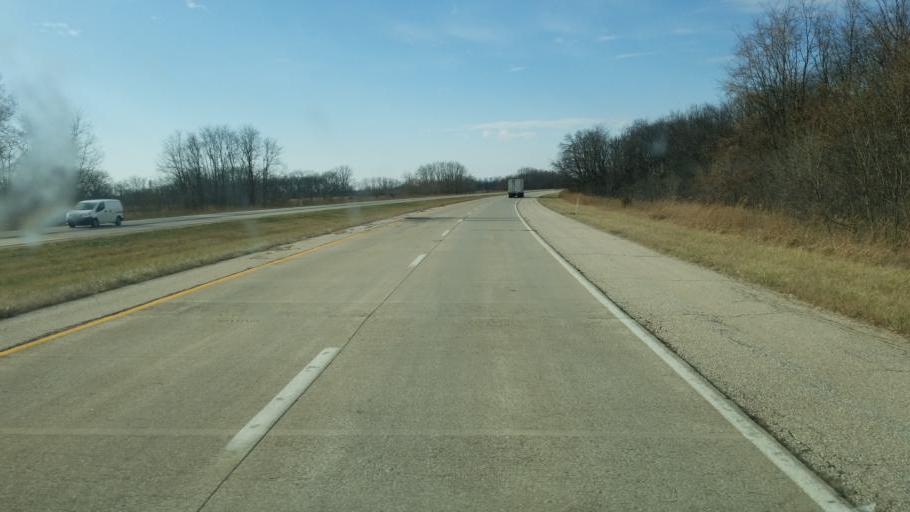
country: US
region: Illinois
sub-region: Knox County
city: Galesburg
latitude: 40.9159
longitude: -90.4846
